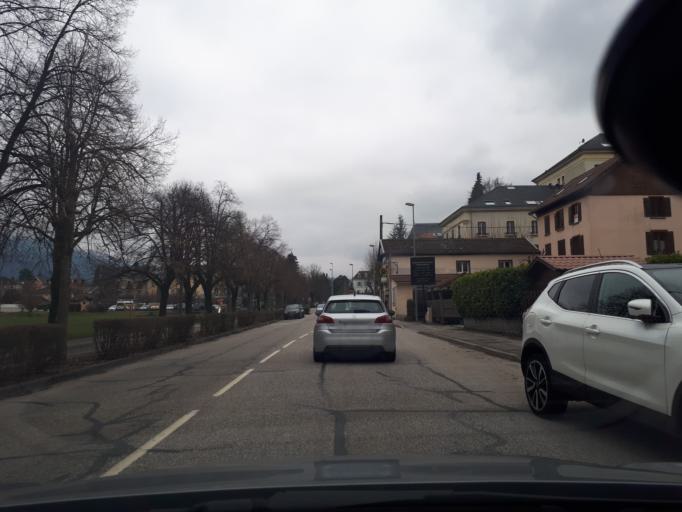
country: FR
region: Rhone-Alpes
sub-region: Departement de l'Isere
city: Vaulnaveys-le-Haut
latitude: 45.1376
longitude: 5.8256
